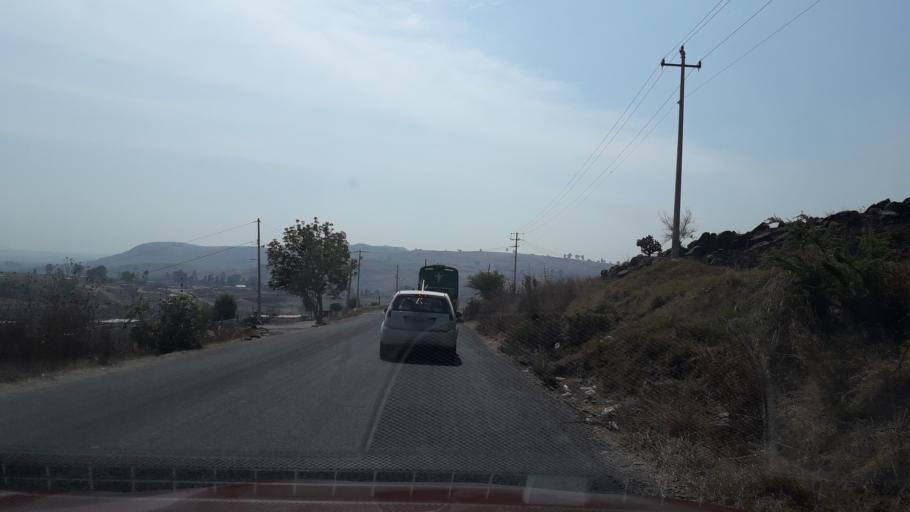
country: MX
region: Puebla
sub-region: Puebla
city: El Capulo (La Quebradora)
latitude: 18.9314
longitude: -98.2604
